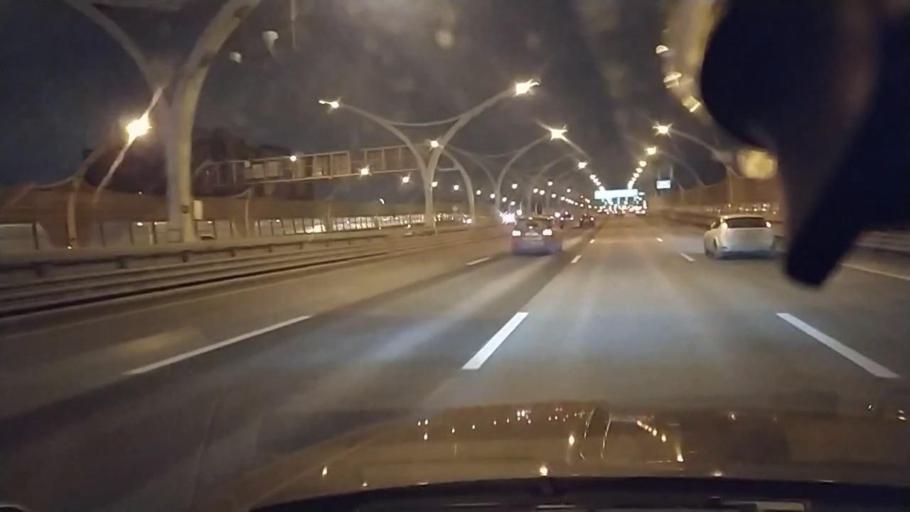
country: RU
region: St.-Petersburg
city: Staraya Derevnya
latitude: 59.9887
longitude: 30.2307
